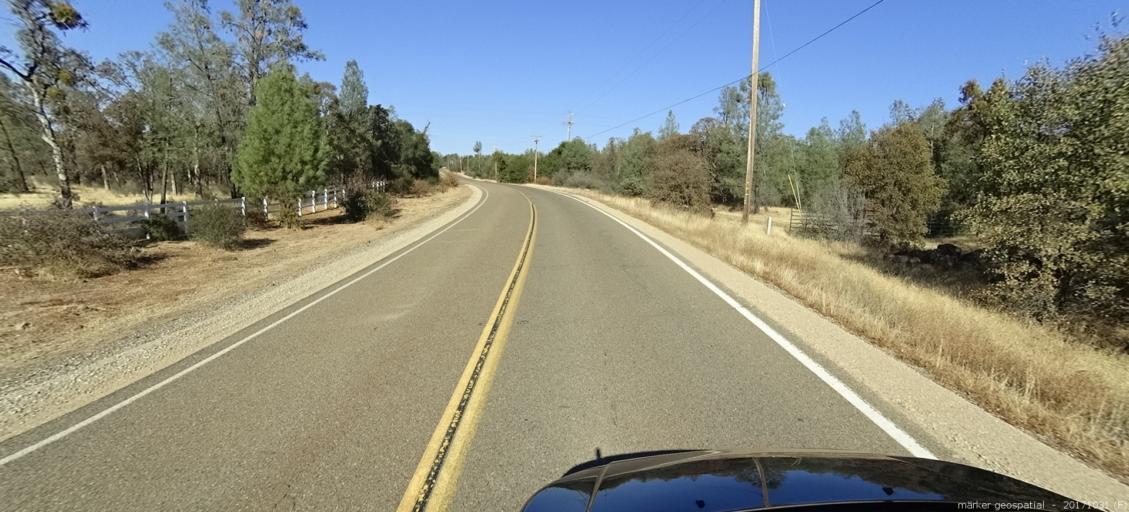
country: US
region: California
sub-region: Shasta County
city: Shingletown
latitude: 40.5004
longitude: -122.0402
